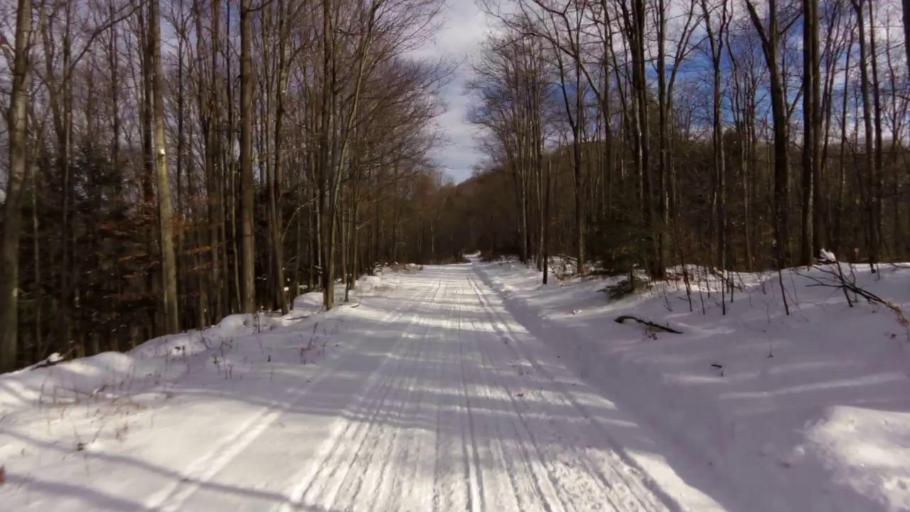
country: US
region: Pennsylvania
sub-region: McKean County
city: Foster Brook
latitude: 42.0096
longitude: -78.6000
